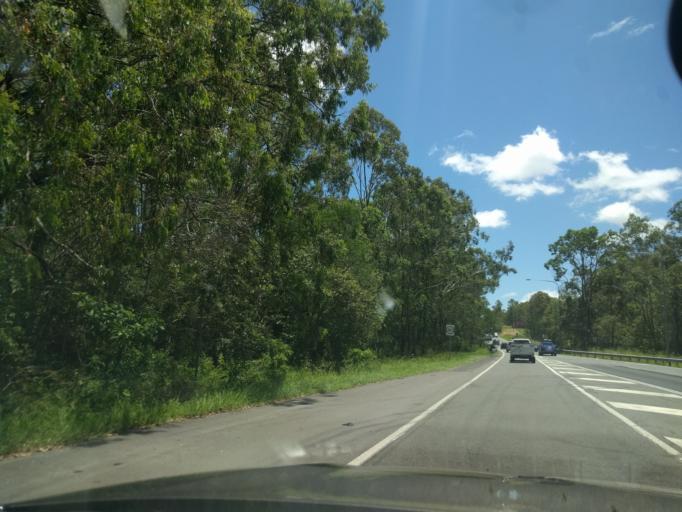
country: AU
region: Queensland
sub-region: Logan
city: Cedar Vale
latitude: -27.8441
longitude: 153.0219
